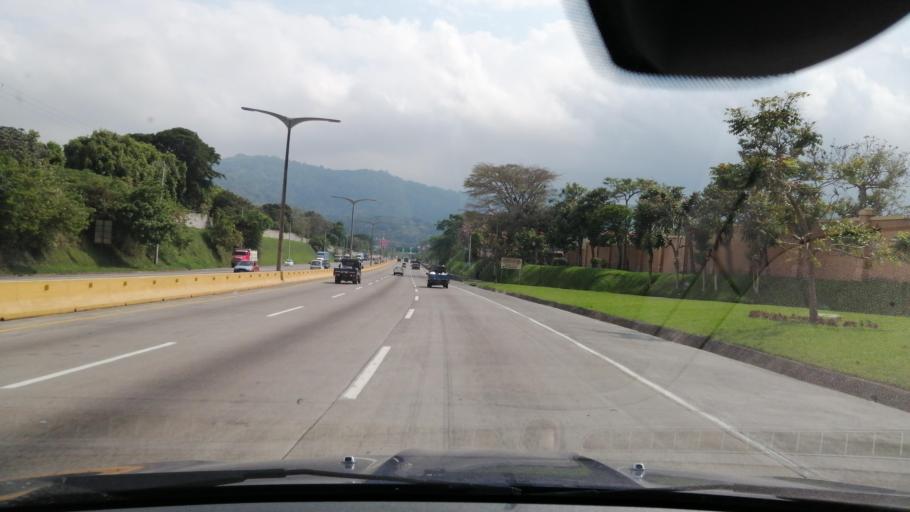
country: SV
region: La Libertad
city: Santa Tecla
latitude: 13.6851
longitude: -89.2968
